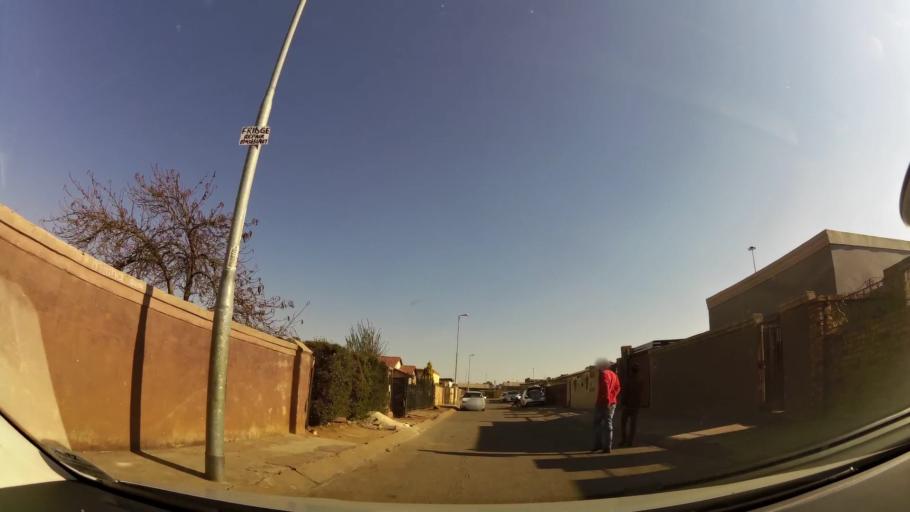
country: ZA
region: Gauteng
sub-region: City of Johannesburg Metropolitan Municipality
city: Soweto
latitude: -26.2771
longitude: 27.8797
